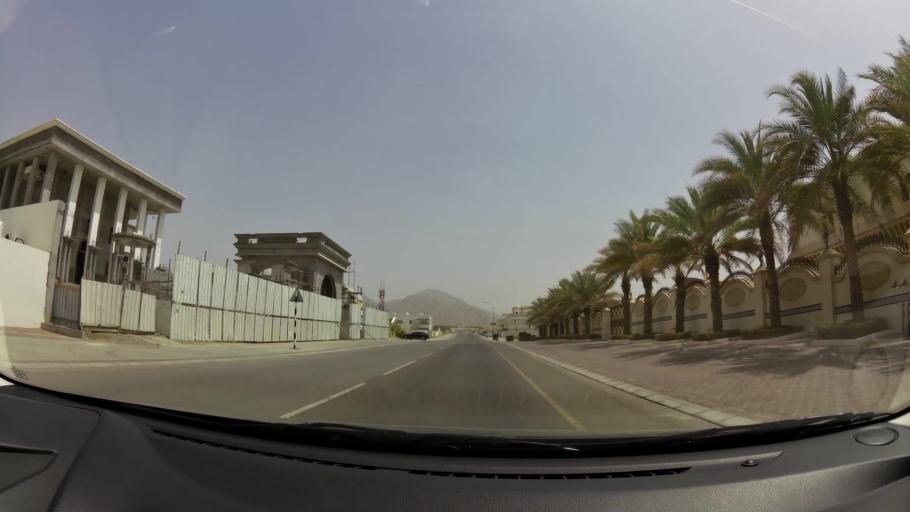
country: OM
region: Muhafazat Masqat
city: Bawshar
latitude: 23.5591
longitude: 58.3942
